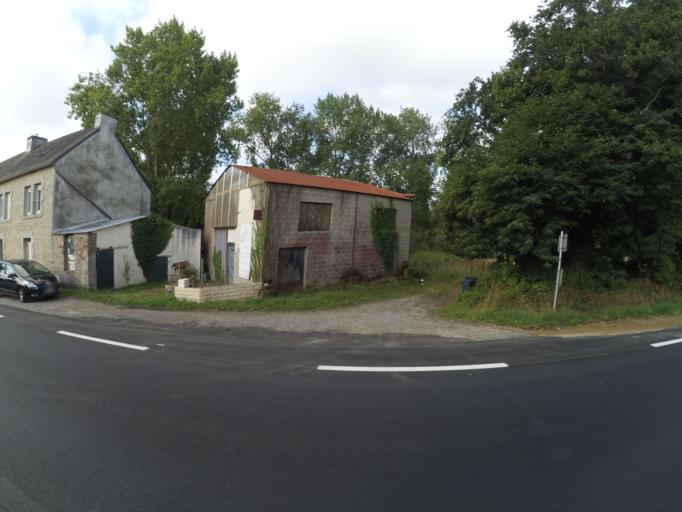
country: FR
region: Brittany
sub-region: Departement du Finistere
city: Redene
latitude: 47.8253
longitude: -3.4928
